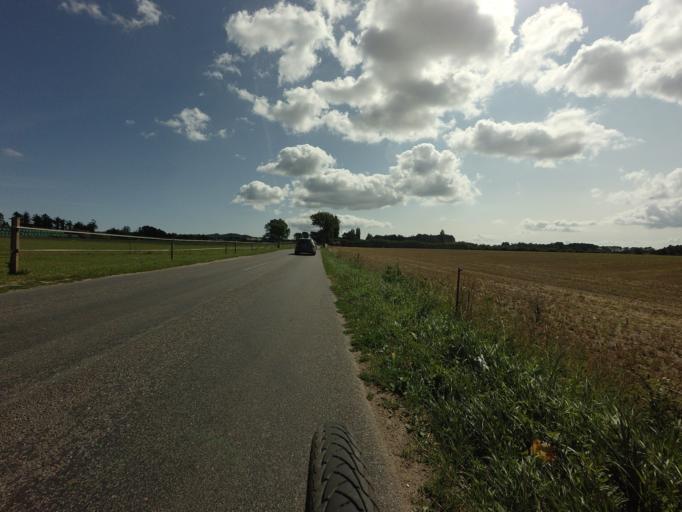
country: DK
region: Zealand
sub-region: Vordingborg Kommune
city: Stege
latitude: 54.9737
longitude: 12.4520
